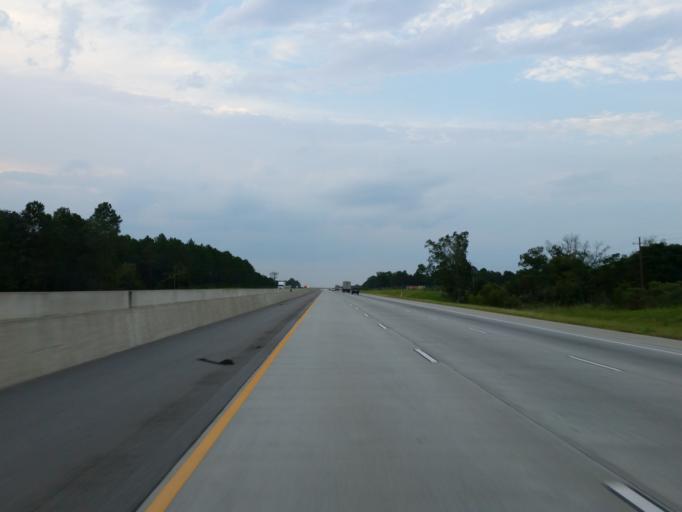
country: US
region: Georgia
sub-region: Tift County
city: Omega
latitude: 31.3194
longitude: -83.4800
